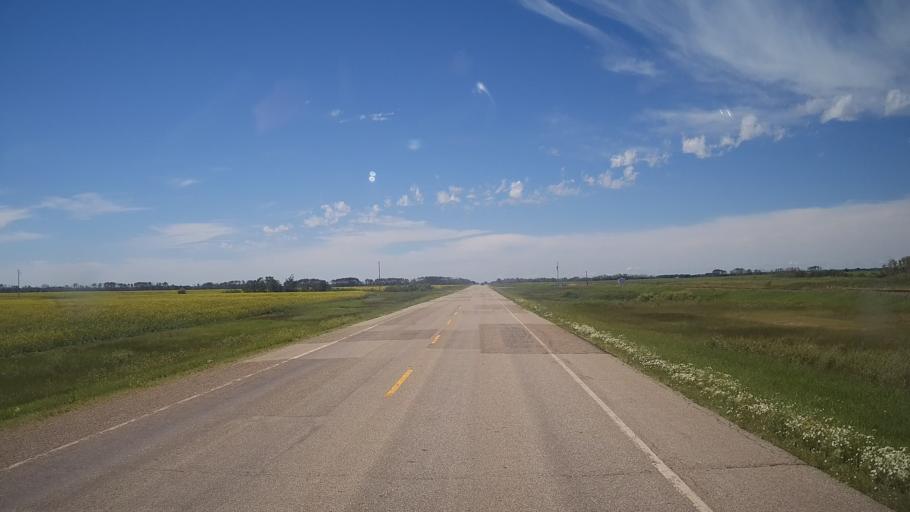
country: CA
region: Saskatchewan
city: Langenburg
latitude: 50.7839
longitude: -101.5284
